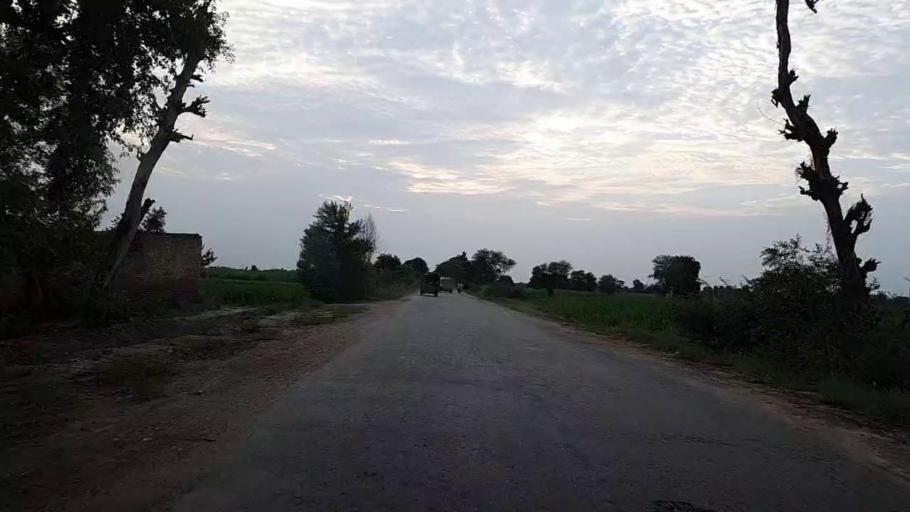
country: PK
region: Sindh
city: Pad Idan
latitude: 26.8051
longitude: 68.2127
